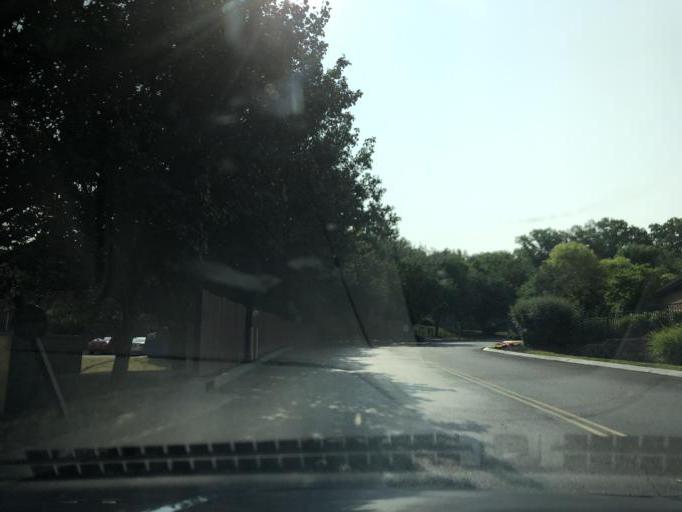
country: US
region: Tennessee
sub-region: Rutherford County
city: La Vergne
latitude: 36.0450
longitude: -86.6402
